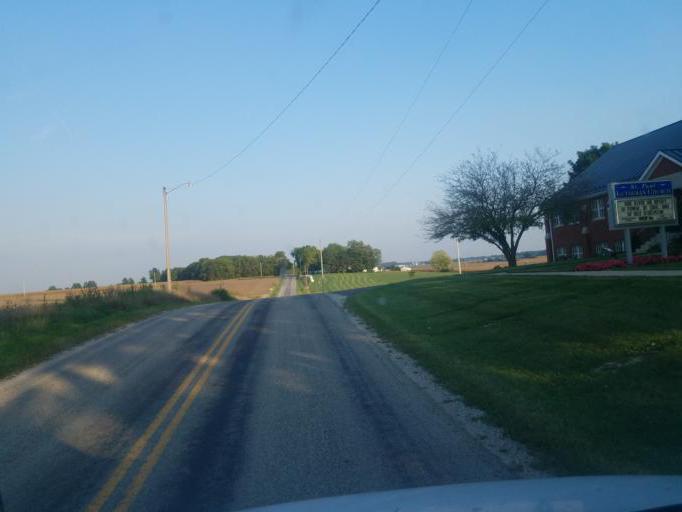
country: US
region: Ohio
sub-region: Crawford County
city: Bucyrus
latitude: 40.8956
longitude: -82.8872
